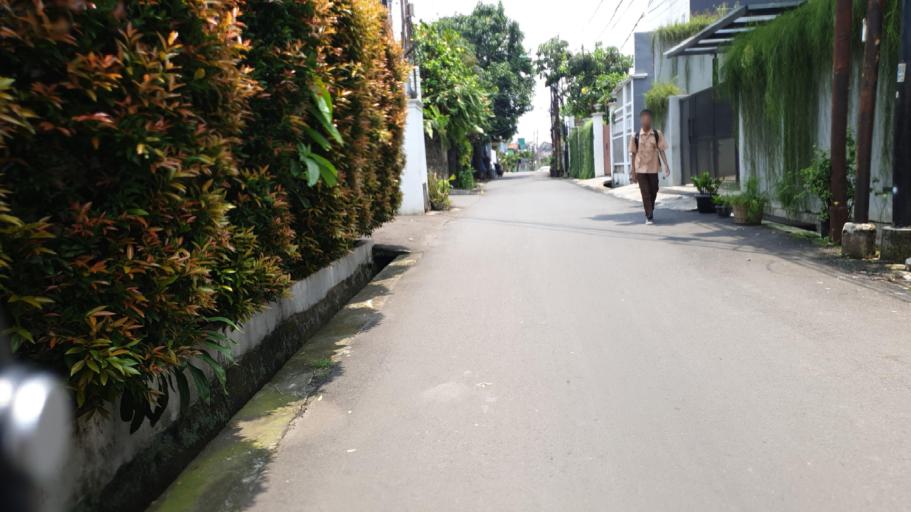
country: ID
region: West Java
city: Pamulang
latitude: -6.3010
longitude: 106.7752
